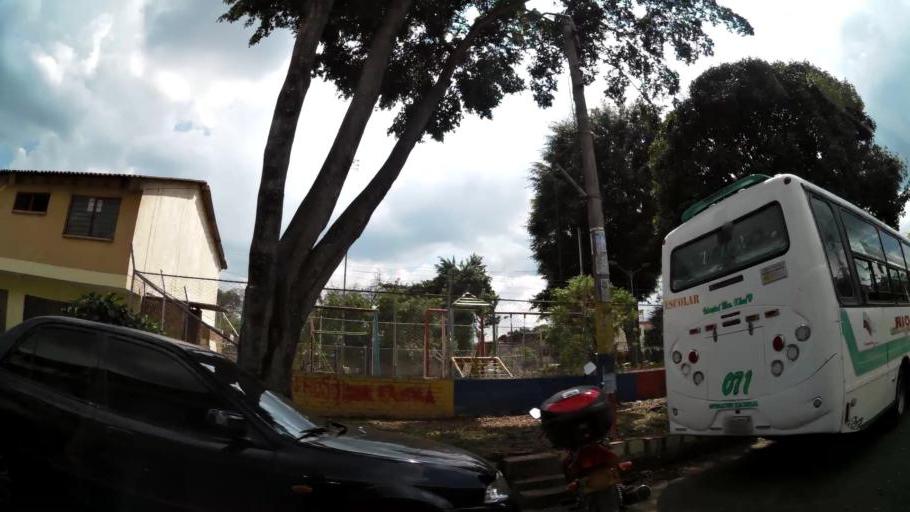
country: CO
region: Valle del Cauca
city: Cali
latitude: 3.4859
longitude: -76.5023
